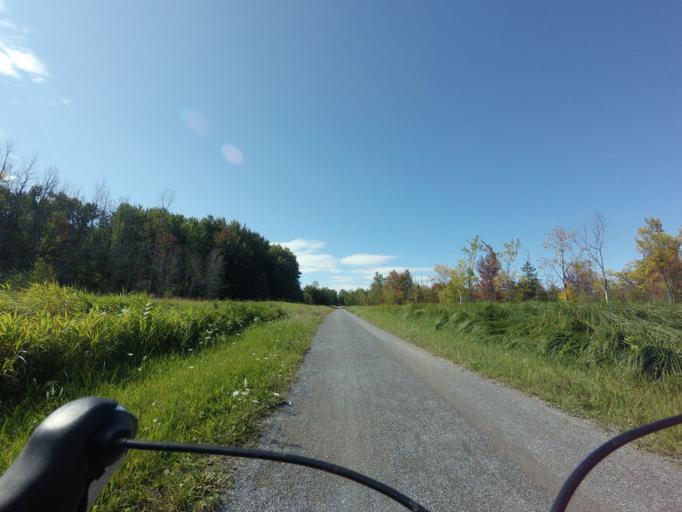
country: CA
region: Ontario
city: Bells Corners
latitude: 45.3137
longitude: -75.8488
